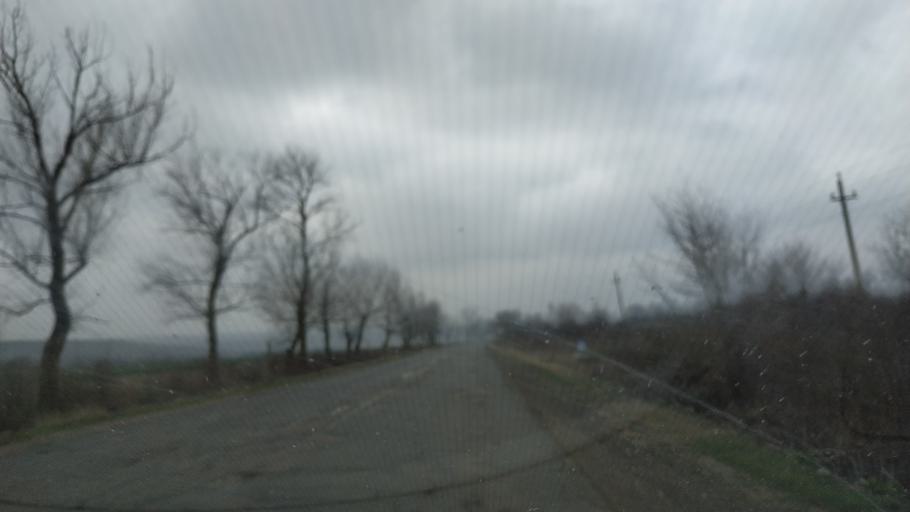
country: MD
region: Gagauzia
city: Bugeac
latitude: 46.3431
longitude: 28.7728
